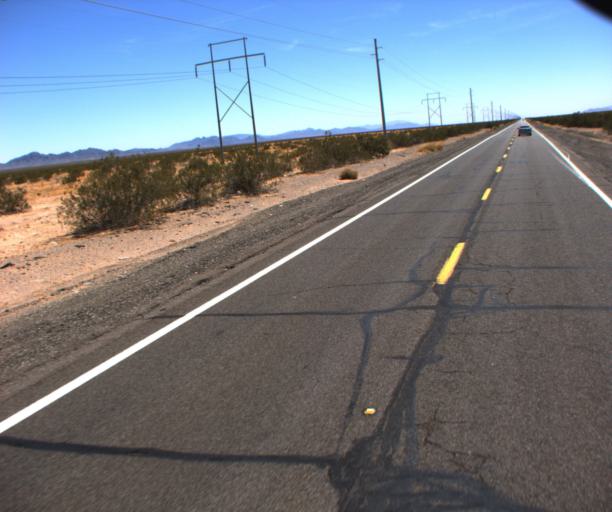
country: US
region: Arizona
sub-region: La Paz County
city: Parker
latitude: 33.9356
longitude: -114.2169
